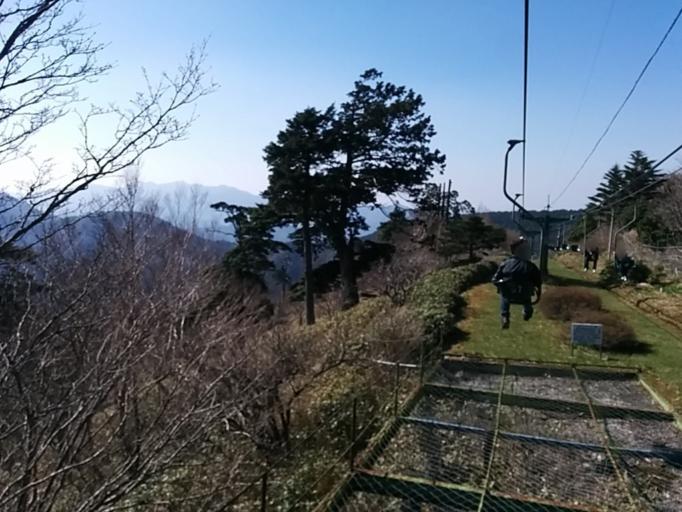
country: JP
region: Tokushima
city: Wakimachi
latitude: 33.8622
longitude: 134.0914
